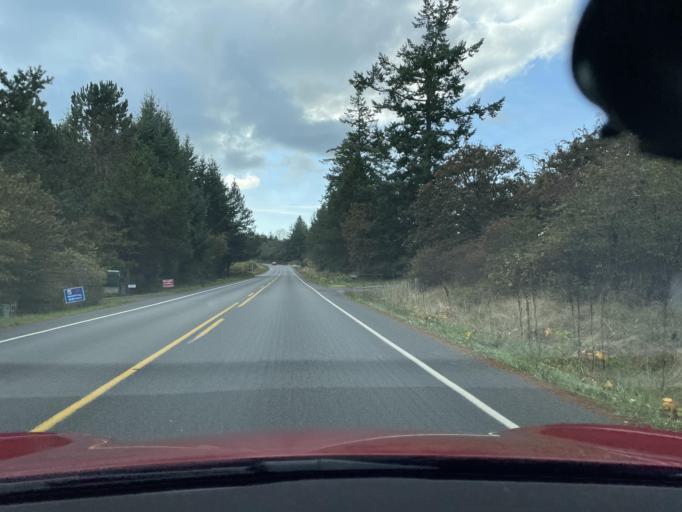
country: US
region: Washington
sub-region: San Juan County
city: Friday Harbor
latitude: 48.5057
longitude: -123.0362
